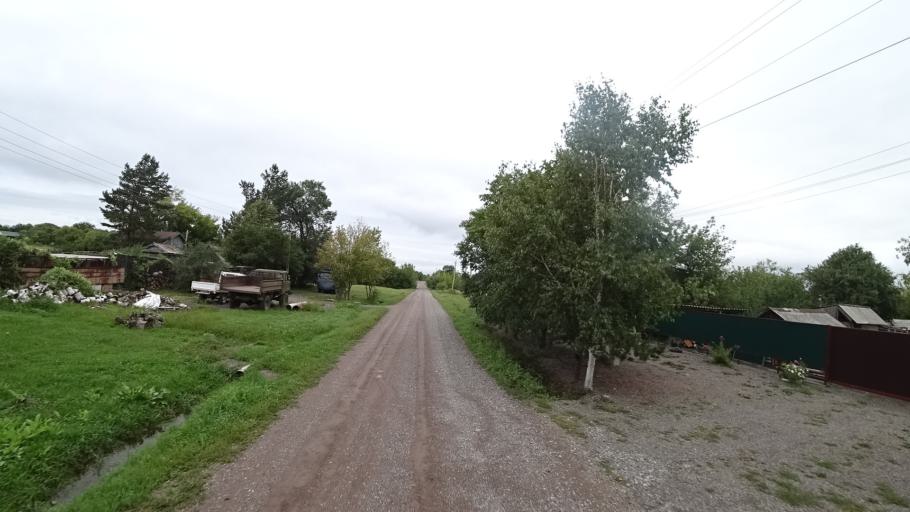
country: RU
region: Primorskiy
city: Chernigovka
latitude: 44.3325
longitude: 132.6000
